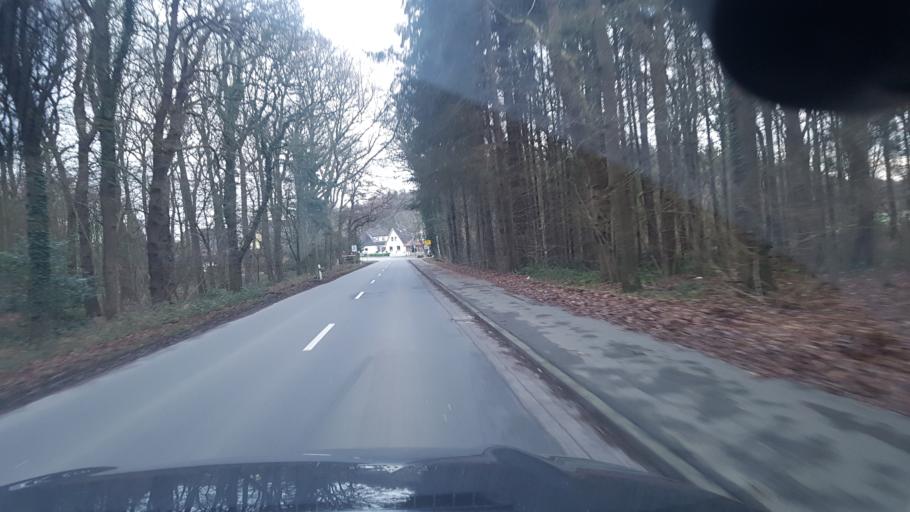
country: DE
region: Lower Saxony
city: Langen
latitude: 53.6085
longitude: 8.6660
